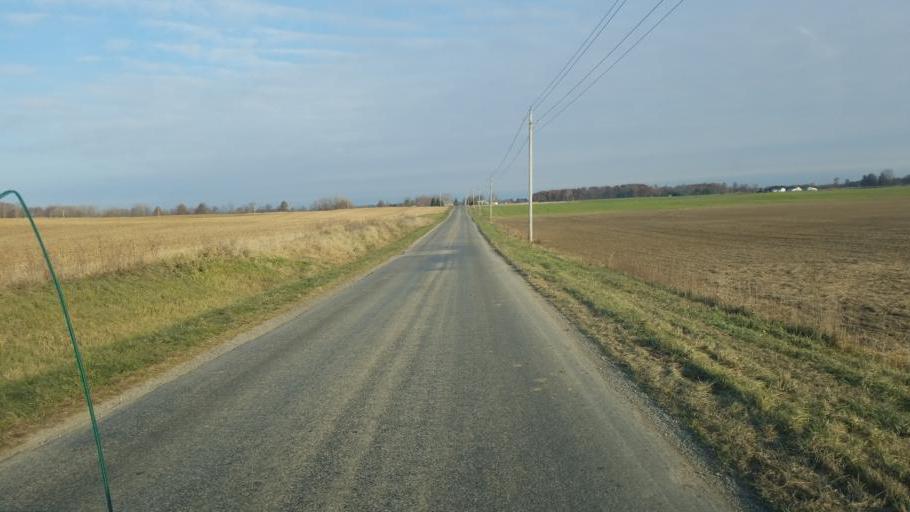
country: US
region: Indiana
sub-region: Adams County
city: Geneva
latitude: 40.5714
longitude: -84.9922
